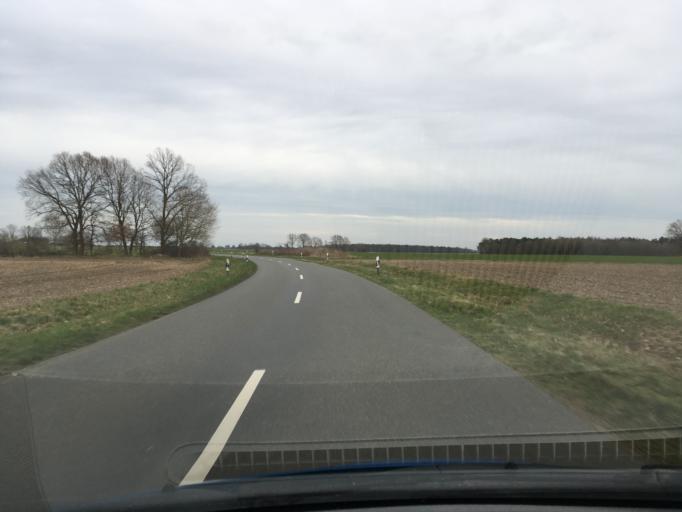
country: DE
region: Lower Saxony
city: Oetzen
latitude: 52.9993
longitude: 10.6242
